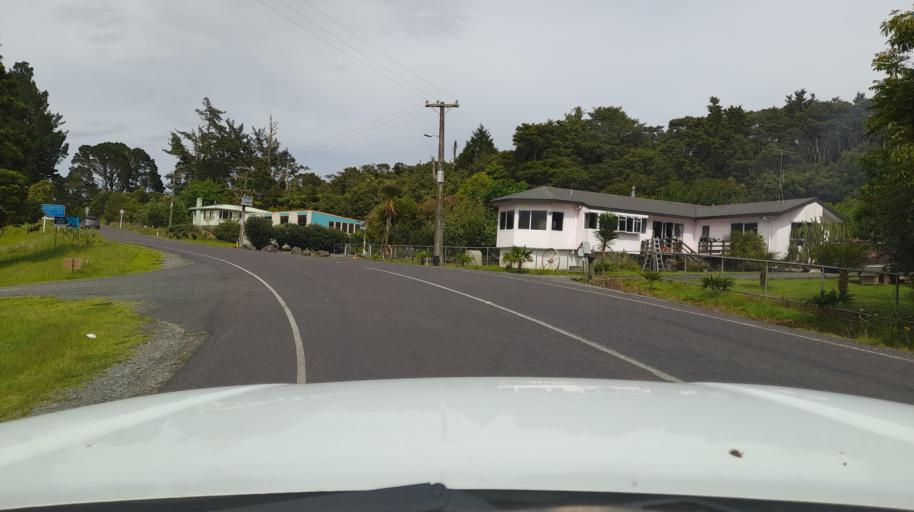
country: NZ
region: Northland
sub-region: Far North District
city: Taipa
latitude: -35.2369
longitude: 173.5437
